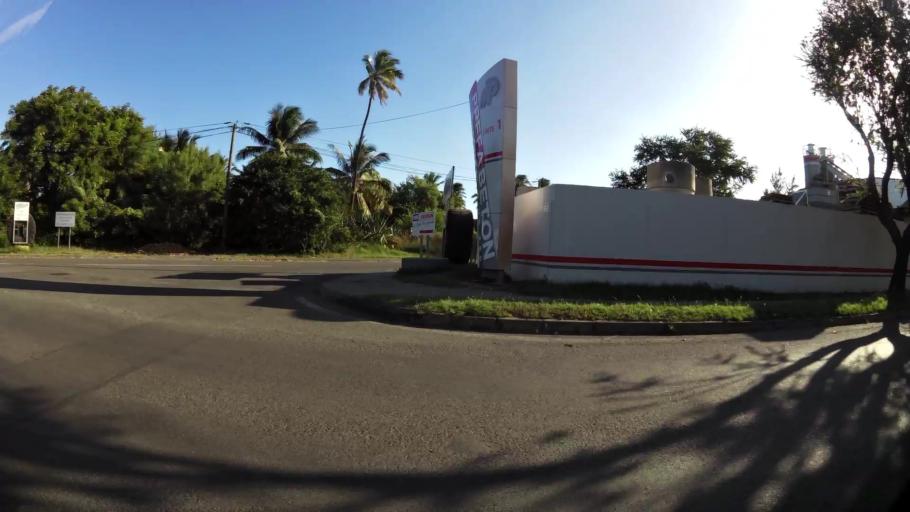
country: RE
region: Reunion
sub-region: Reunion
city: Saint-Louis
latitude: -21.2784
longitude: 55.3735
